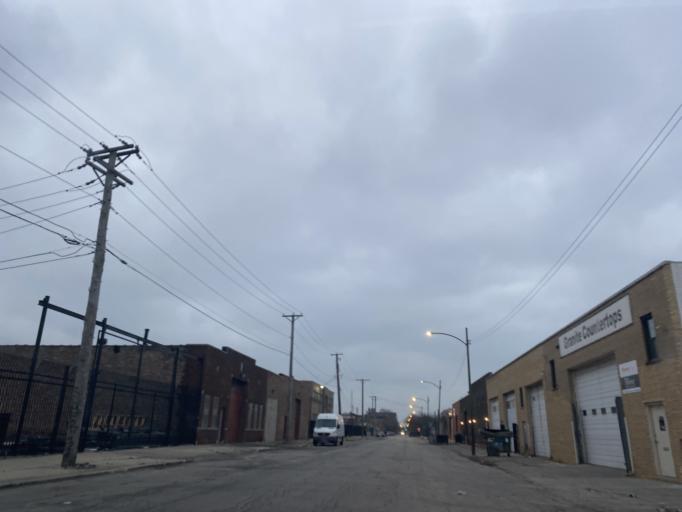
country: US
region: Illinois
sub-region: Cook County
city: Chicago
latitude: 41.8897
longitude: -87.6772
